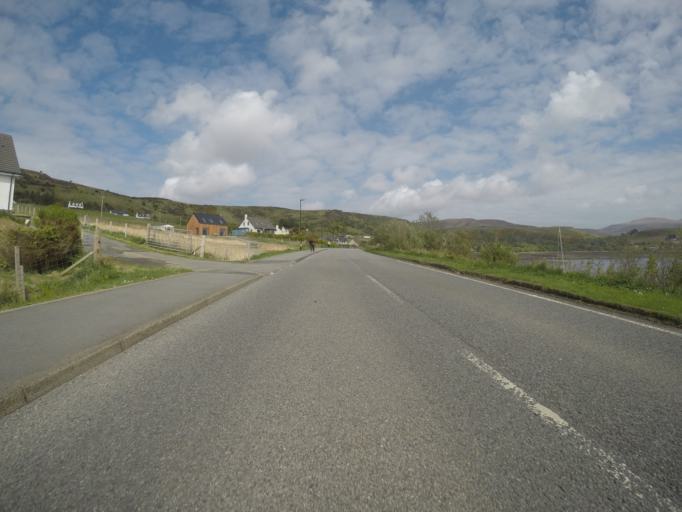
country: GB
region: Scotland
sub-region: Highland
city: Portree
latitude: 57.5885
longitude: -6.3751
